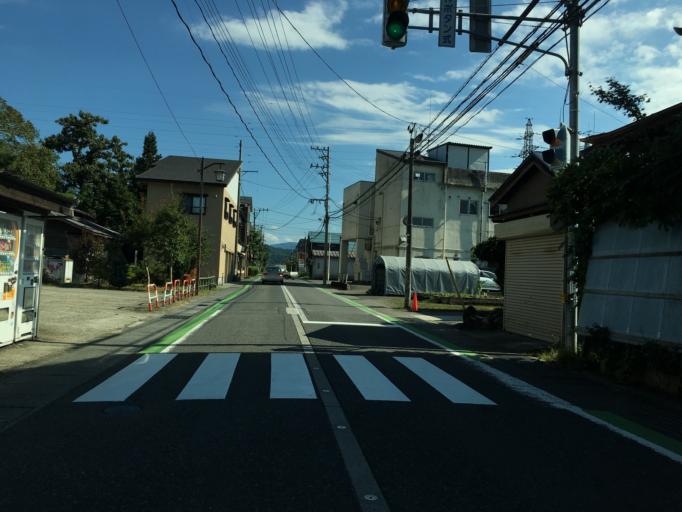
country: JP
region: Niigata
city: Suibara
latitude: 37.6760
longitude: 139.4631
